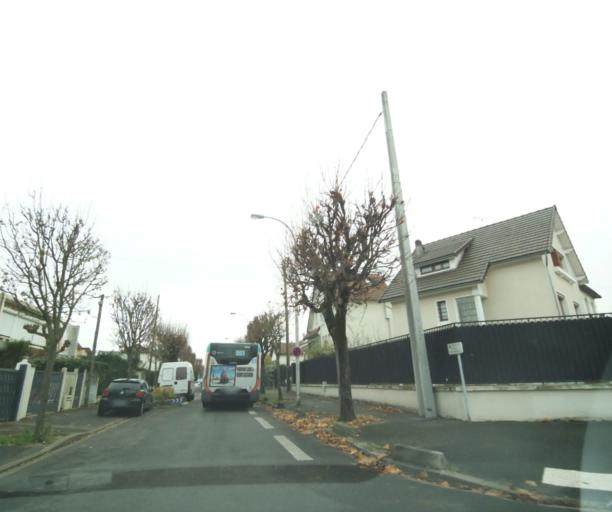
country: FR
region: Ile-de-France
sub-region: Departement de Seine-Saint-Denis
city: Villemomble
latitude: 48.8877
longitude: 2.4981
